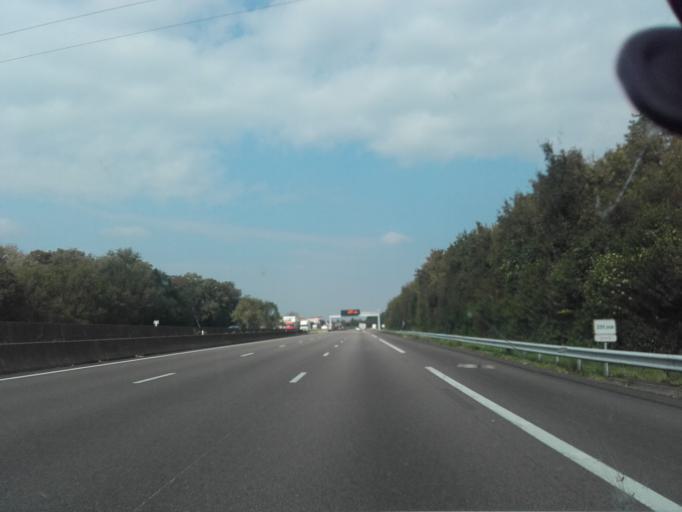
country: FR
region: Bourgogne
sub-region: Departement de Saone-et-Loire
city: Chatenoy-le-Royal
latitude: 46.7836
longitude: 4.8199
